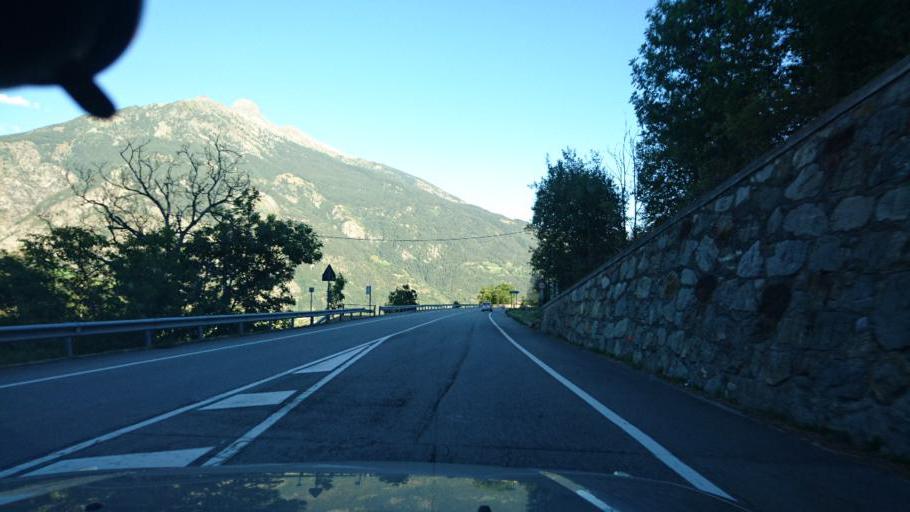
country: IT
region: Aosta Valley
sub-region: Valle d'Aosta
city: Allein
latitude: 45.7964
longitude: 7.2817
